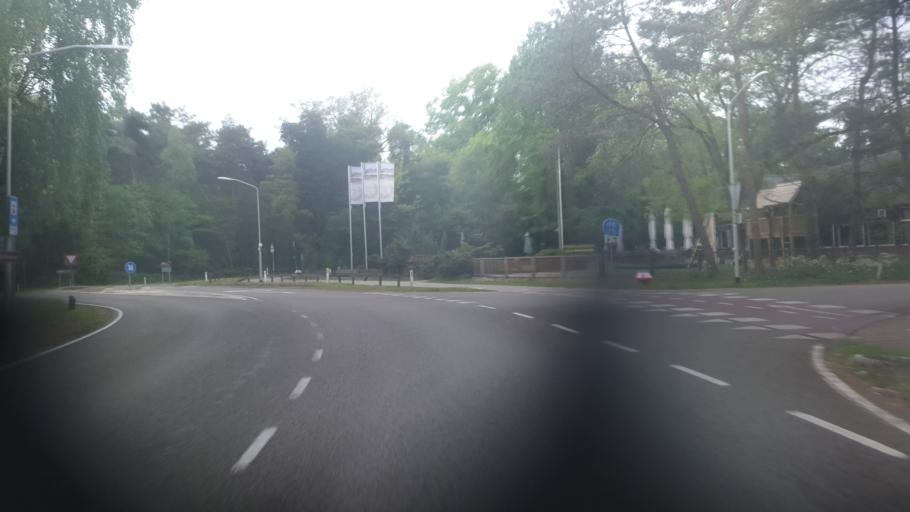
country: NL
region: Gelderland
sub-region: Gemeente Nijmegen
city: Lindenholt
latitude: 51.7815
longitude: 5.7962
